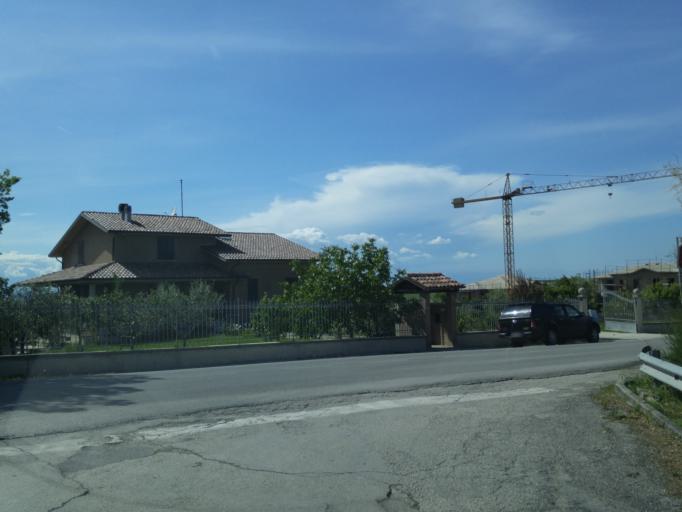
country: IT
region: The Marches
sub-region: Provincia di Pesaro e Urbino
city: San Costanzo
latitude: 43.7728
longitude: 13.0754
